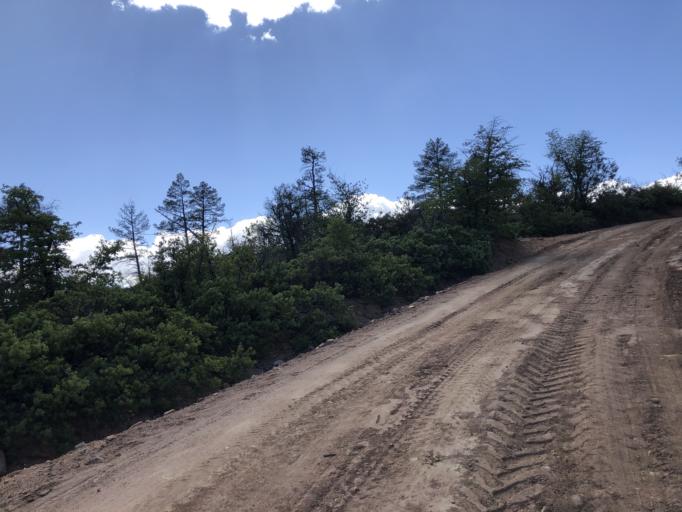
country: US
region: Arizona
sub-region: Gila County
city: Star Valley
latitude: 34.3529
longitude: -111.2785
